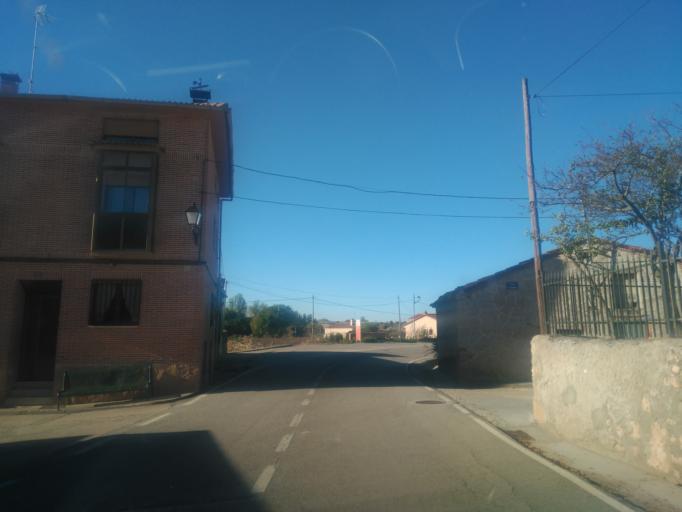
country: ES
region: Castille and Leon
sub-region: Provincia de Burgos
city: Brazacorta
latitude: 41.7195
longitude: -3.3441
